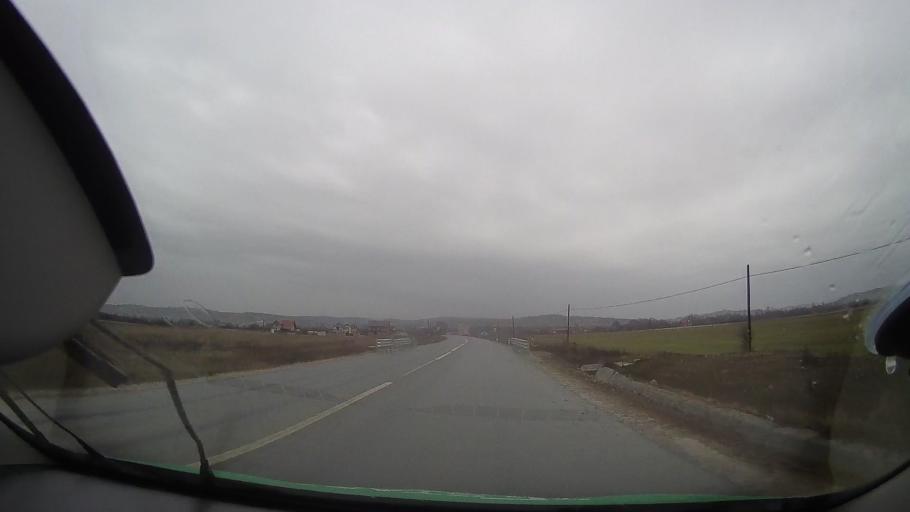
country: RO
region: Bihor
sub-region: Comuna Pocola
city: Pocola
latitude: 46.6899
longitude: 22.2989
